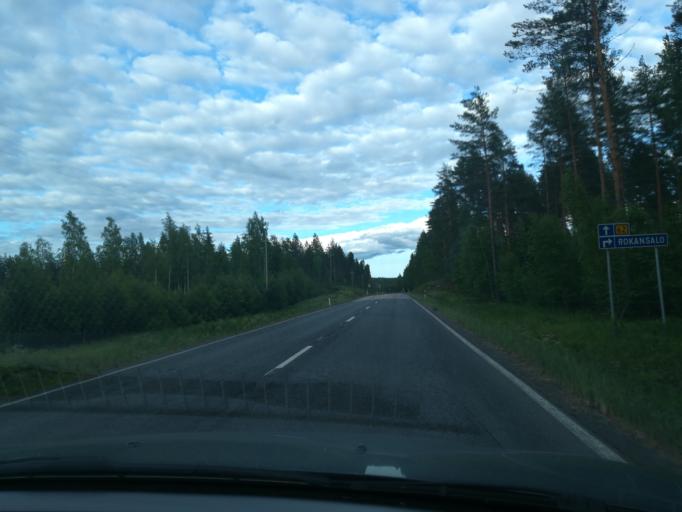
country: FI
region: Southern Savonia
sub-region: Mikkeli
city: Puumala
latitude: 61.5601
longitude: 28.0220
